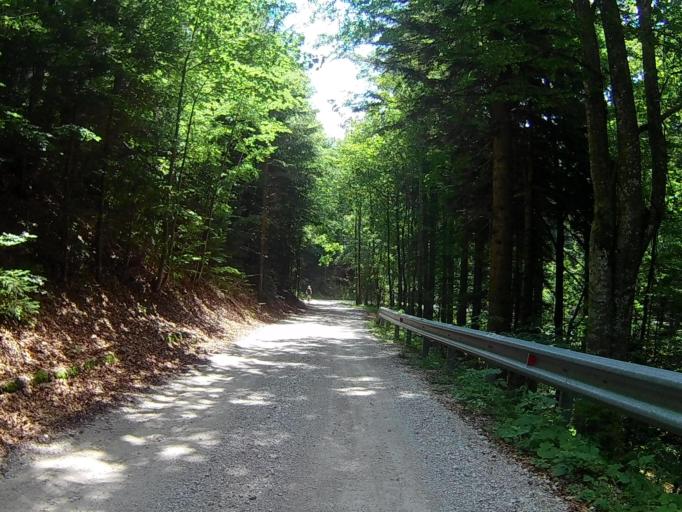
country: SI
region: Selnica ob Dravi
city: Selnica ob Dravi
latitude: 46.4862
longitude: 15.4575
